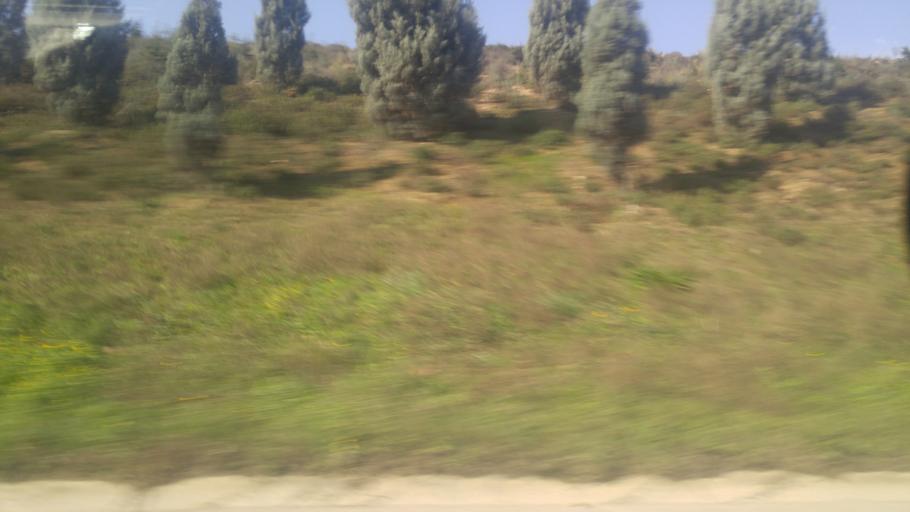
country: TR
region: Kocaeli
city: Balcik
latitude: 40.8477
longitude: 29.3747
